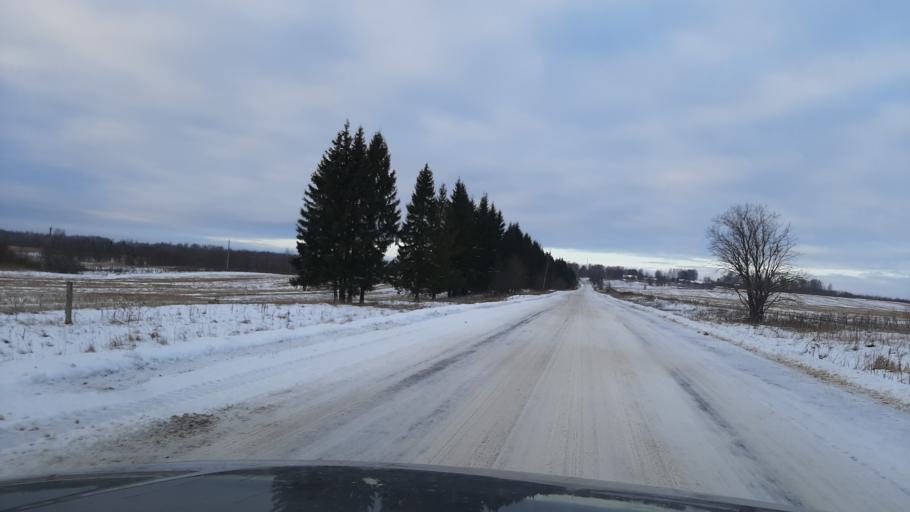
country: RU
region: Kostroma
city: Kosmynino
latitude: 57.4821
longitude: 40.7876
